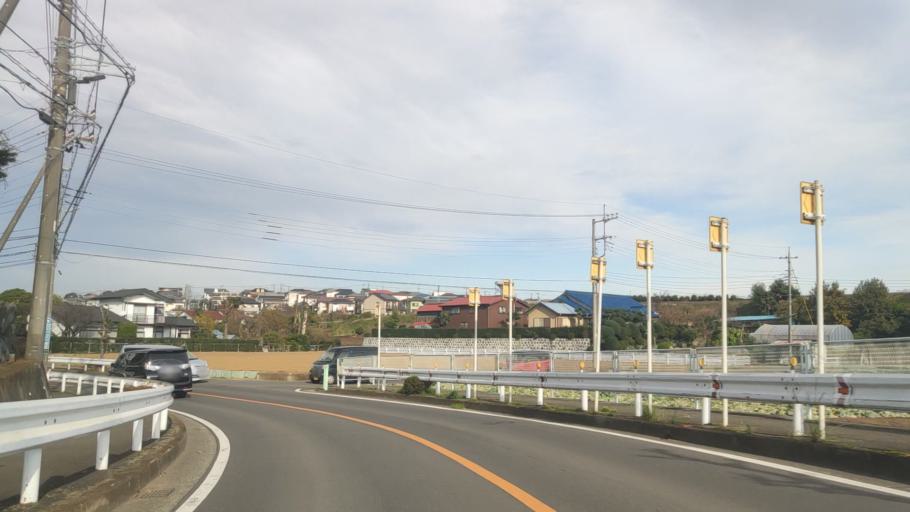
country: JP
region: Kanagawa
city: Atsugi
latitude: 35.4306
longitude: 139.4043
